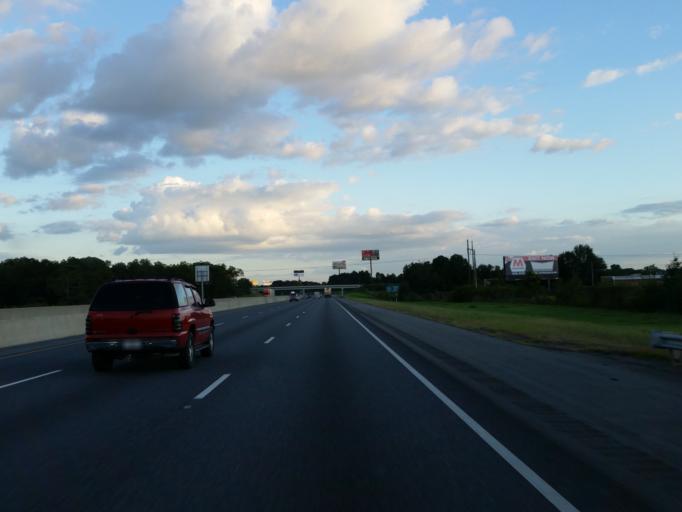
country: US
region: Georgia
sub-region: Turner County
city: Ashburn
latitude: 31.6964
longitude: -83.6306
